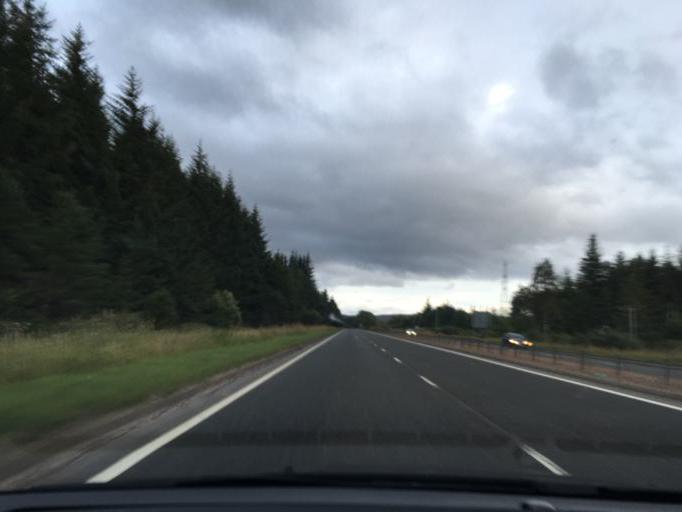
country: GB
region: Scotland
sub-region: Highland
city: Inverness
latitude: 57.4412
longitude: -4.1451
